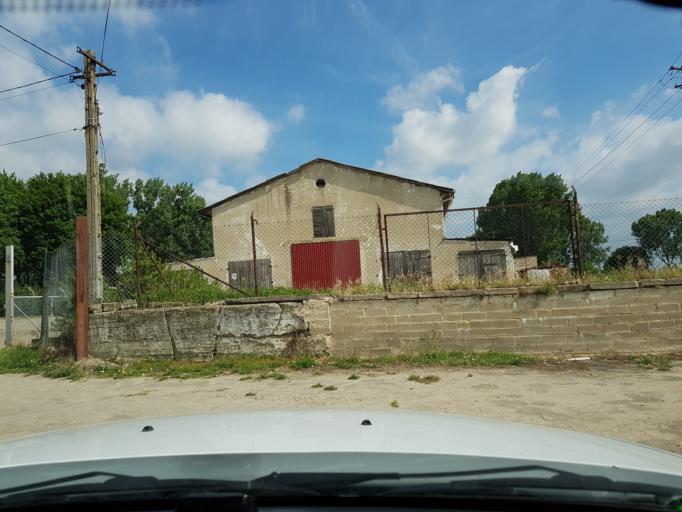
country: PL
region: West Pomeranian Voivodeship
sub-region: Powiat gryfinski
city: Banie
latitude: 53.1262
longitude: 14.5998
